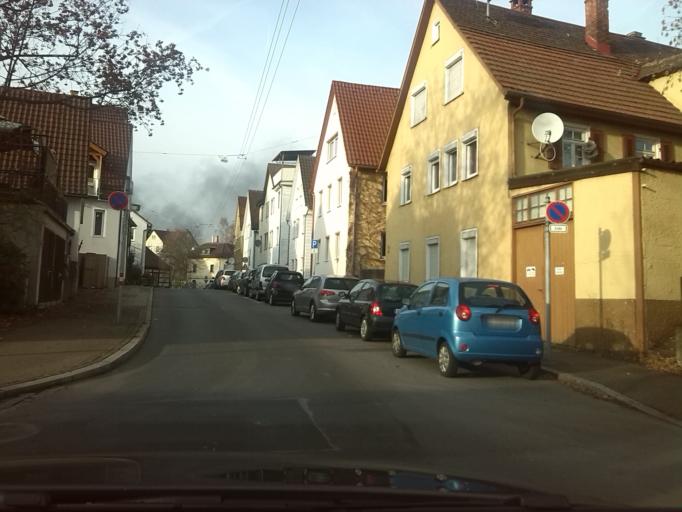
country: DE
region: Baden-Wuerttemberg
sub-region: Regierungsbezirk Stuttgart
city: Fellbach
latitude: 48.7782
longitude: 9.2551
